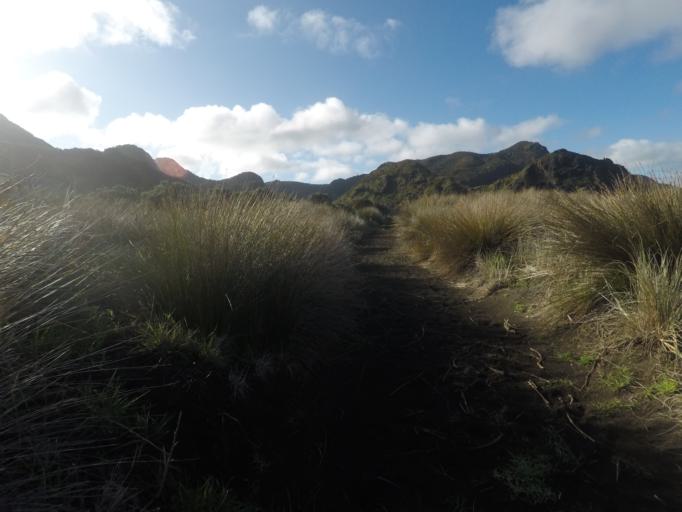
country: NZ
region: Auckland
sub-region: Auckland
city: Titirangi
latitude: -37.0096
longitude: 174.4812
